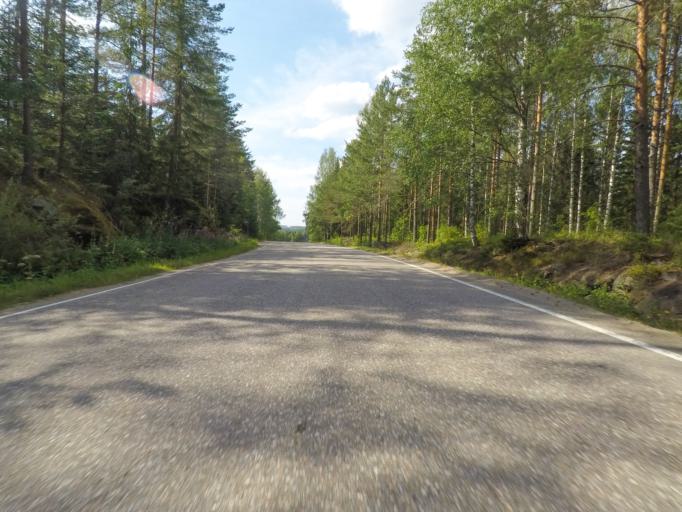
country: FI
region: Southern Savonia
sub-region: Mikkeli
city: Puumala
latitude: 61.6851
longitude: 28.2282
